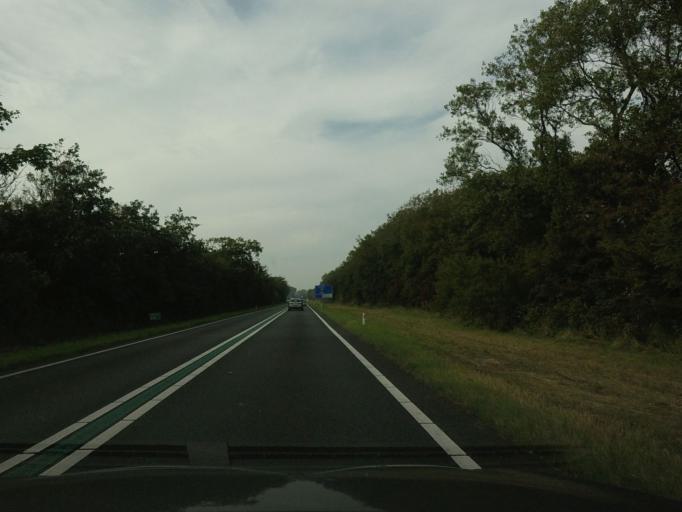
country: NL
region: North Holland
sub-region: Gemeente Den Helder
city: Den Helder
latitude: 52.9098
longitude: 4.8076
